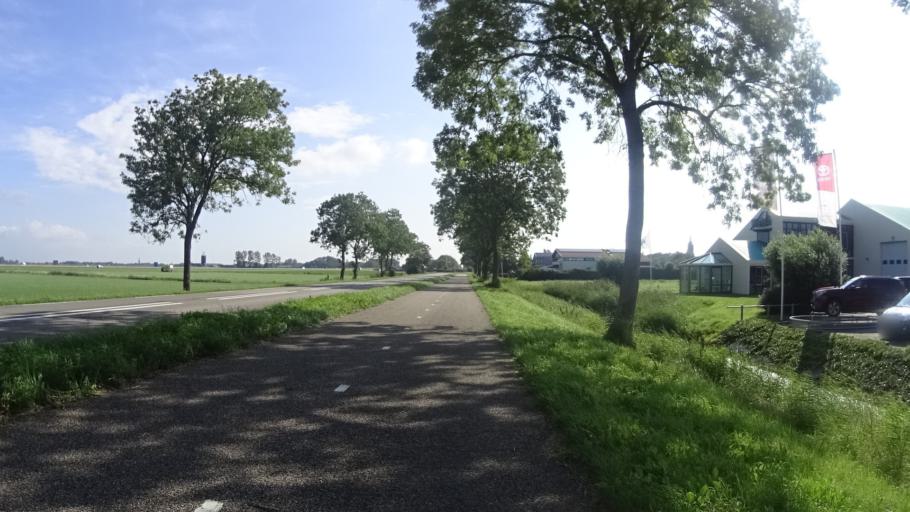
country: NL
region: Friesland
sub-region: Menameradiel
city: Dronryp
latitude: 53.1979
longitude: 5.6331
